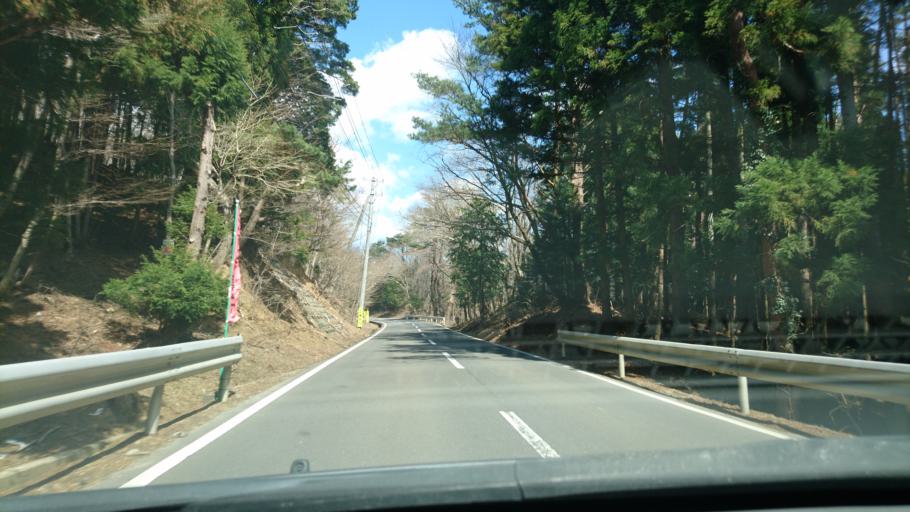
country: JP
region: Miyagi
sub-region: Oshika Gun
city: Onagawa Cho
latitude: 38.4754
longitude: 141.4924
